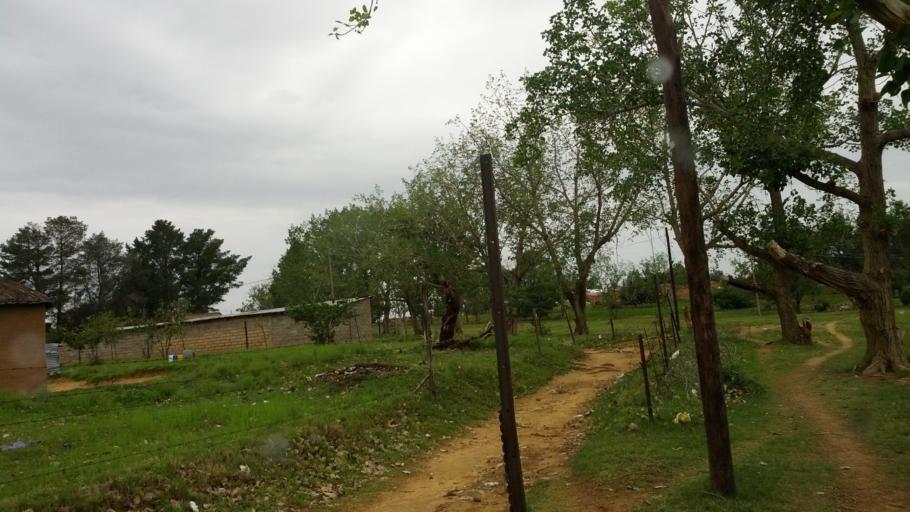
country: LS
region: Berea
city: Teyateyaneng
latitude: -29.1067
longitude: 27.9605
